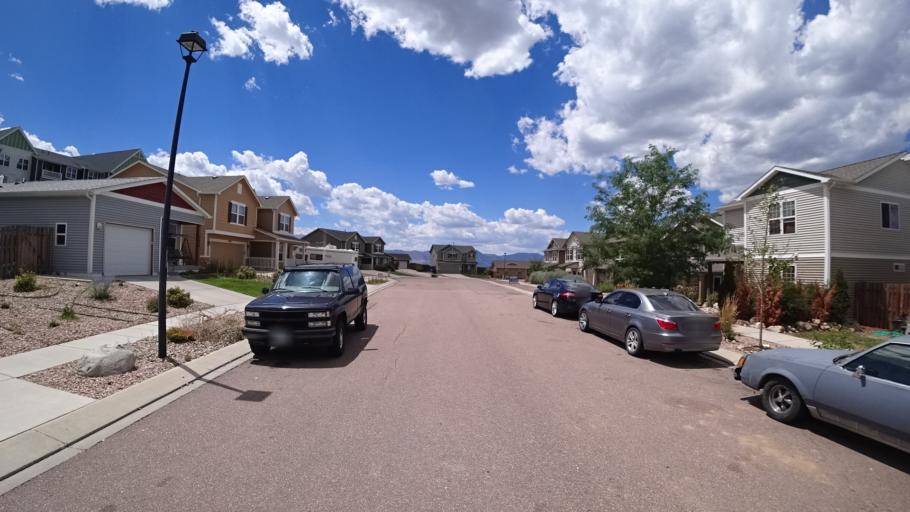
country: US
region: Colorado
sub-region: El Paso County
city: Black Forest
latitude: 38.9445
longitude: -104.7106
